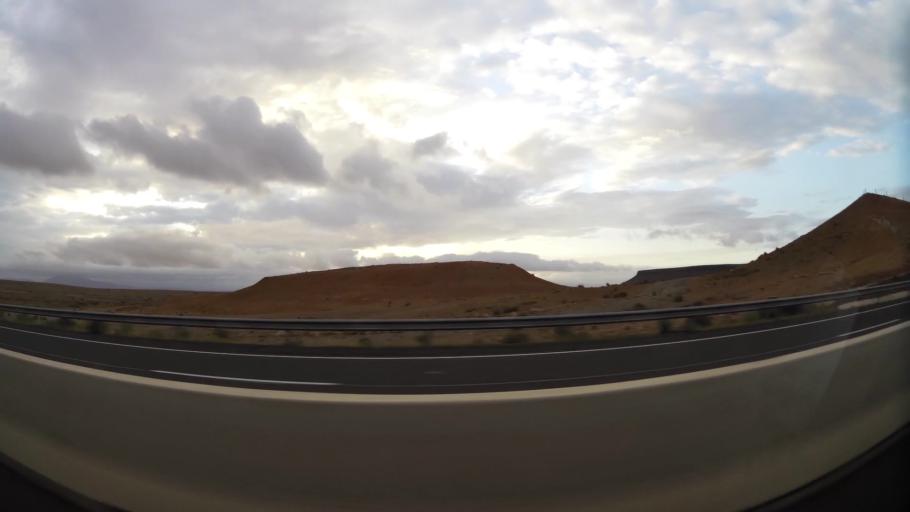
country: MA
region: Oriental
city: Taourirt
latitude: 34.4402
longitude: -3.0817
